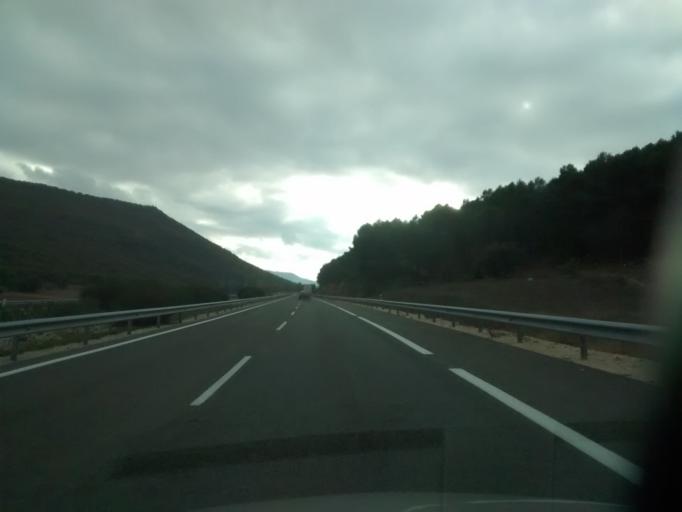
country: ES
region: Castille-La Mancha
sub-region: Provincia de Guadalajara
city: Aldeanueva de Guadalajara
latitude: 40.7106
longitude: -3.0722
